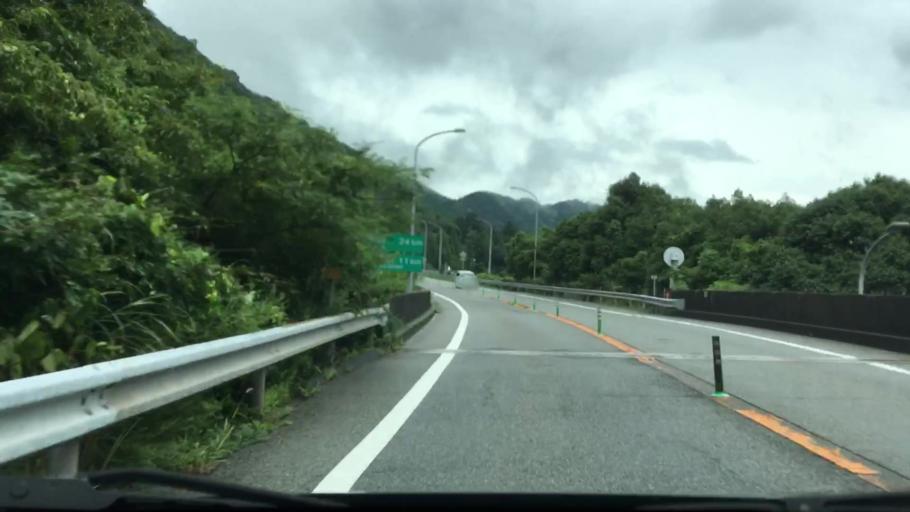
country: JP
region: Hyogo
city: Nishiwaki
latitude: 35.0307
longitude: 134.7660
